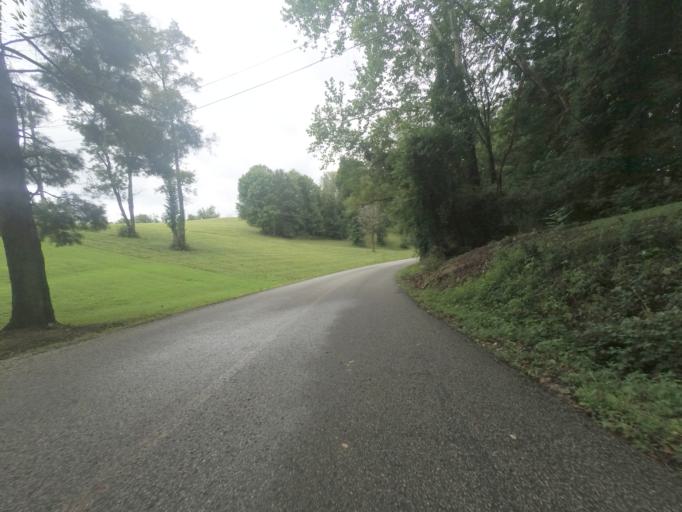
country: US
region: West Virginia
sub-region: Cabell County
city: Huntington
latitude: 38.4304
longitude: -82.4682
